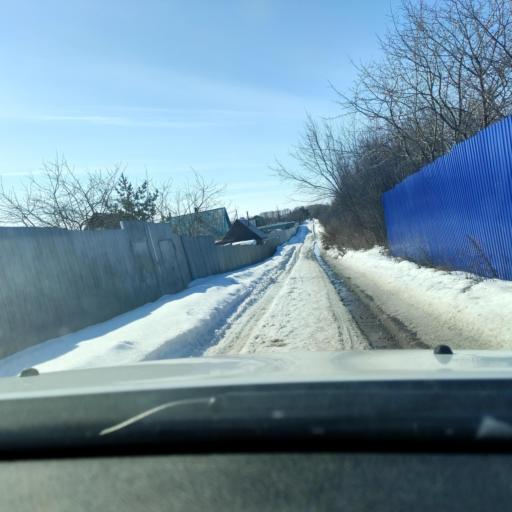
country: RU
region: Bashkortostan
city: Ufa
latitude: 54.5567
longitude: 55.9358
